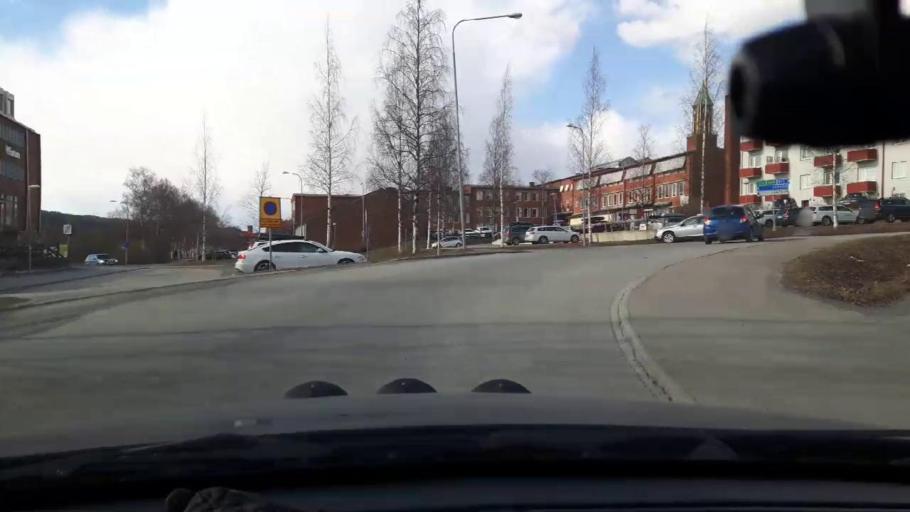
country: SE
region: Jaemtland
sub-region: OEstersunds Kommun
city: Ostersund
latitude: 63.1692
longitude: 14.6421
